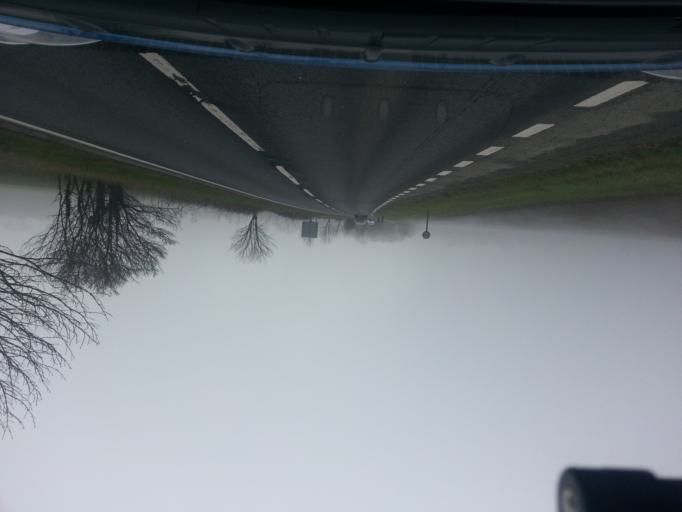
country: GB
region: England
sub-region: Oxfordshire
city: Stanford in the Vale
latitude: 51.6750
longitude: -1.4648
